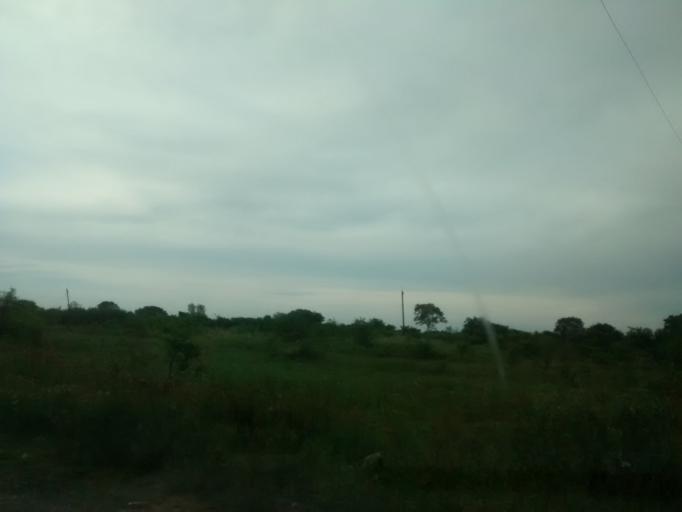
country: AR
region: Chaco
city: Fontana
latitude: -27.4675
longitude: -59.0362
